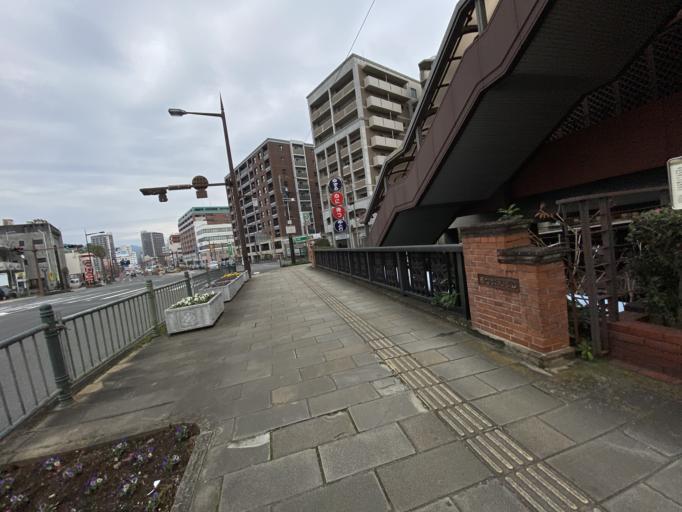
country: JP
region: Nagasaki
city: Nagasaki-shi
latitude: 32.7370
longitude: 129.8700
